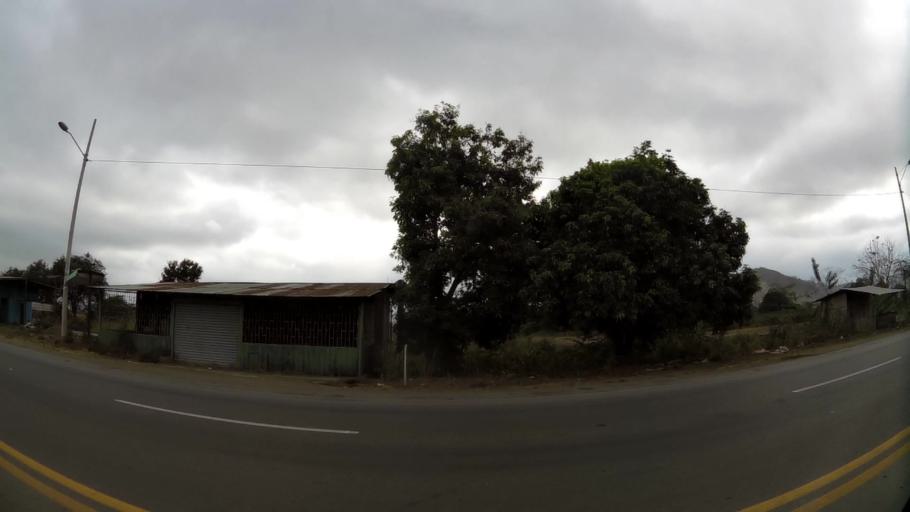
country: EC
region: Guayas
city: Coronel Marcelino Mariduena
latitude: -2.3736
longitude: -79.6321
